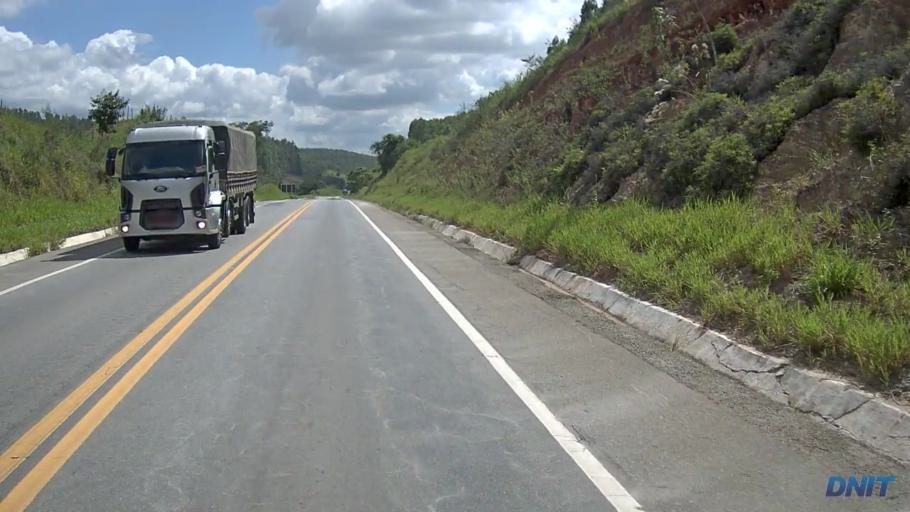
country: BR
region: Minas Gerais
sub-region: Governador Valadares
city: Governador Valadares
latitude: -19.0794
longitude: -42.1812
